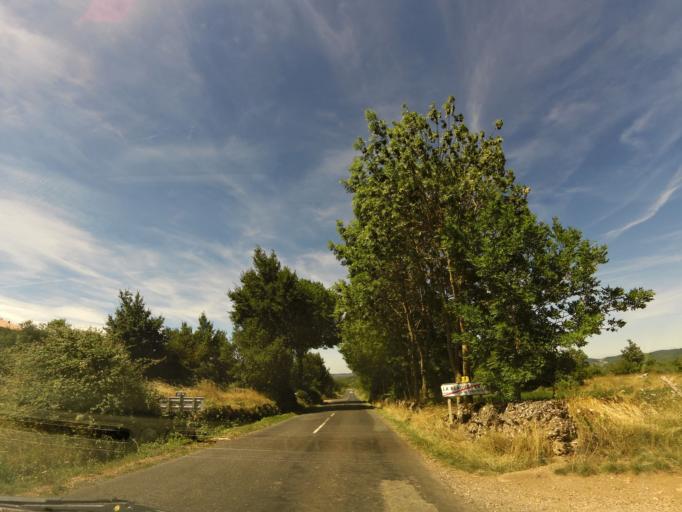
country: FR
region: Midi-Pyrenees
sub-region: Departement de l'Aveyron
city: La Cavalerie
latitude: 43.9506
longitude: 3.2648
